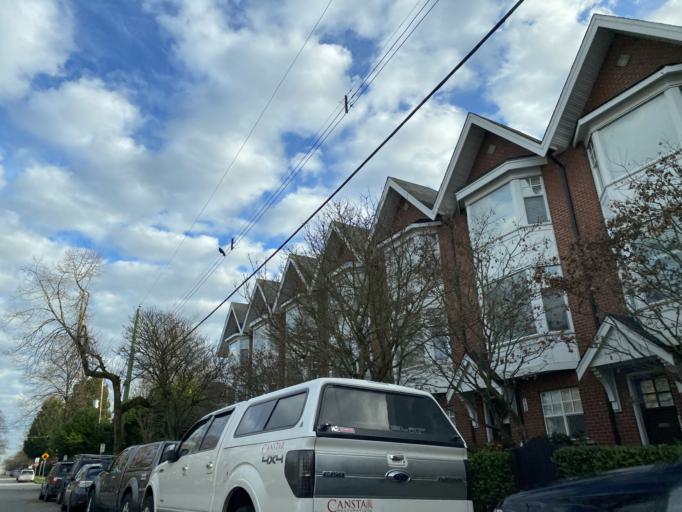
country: CA
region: British Columbia
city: West End
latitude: 49.2648
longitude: -123.1541
